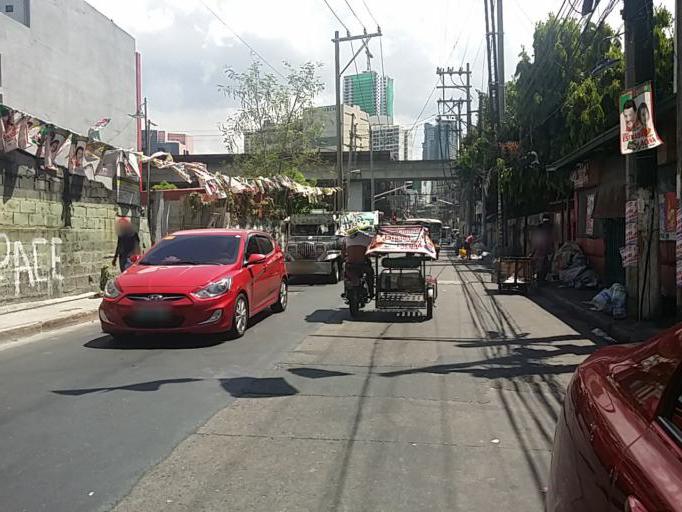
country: PH
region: Metro Manila
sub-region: City of Manila
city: Quiapo
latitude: 14.6010
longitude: 120.9877
